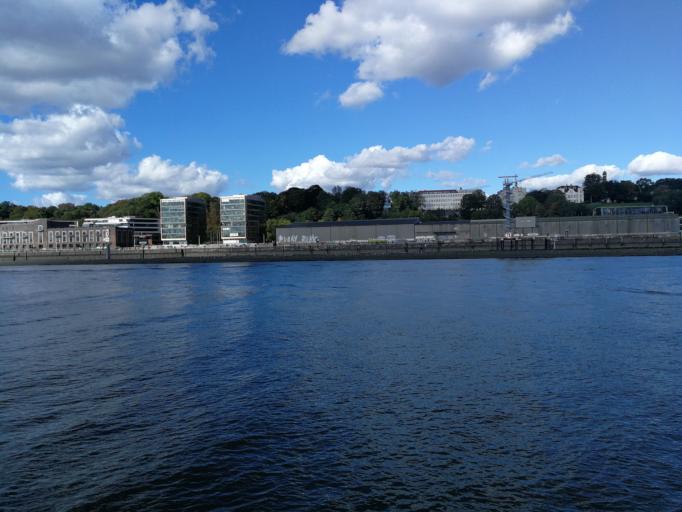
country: DE
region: Hamburg
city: Altona
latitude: 53.5415
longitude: 9.9312
